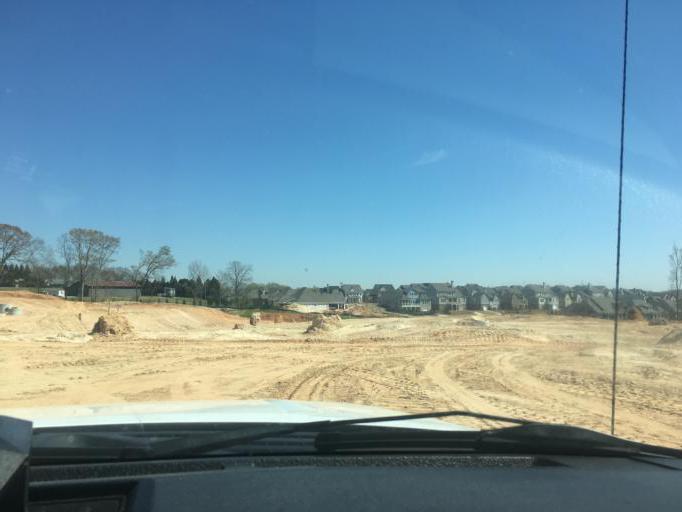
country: US
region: Georgia
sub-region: Jackson County
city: Braselton
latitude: 34.1118
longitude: -83.8442
